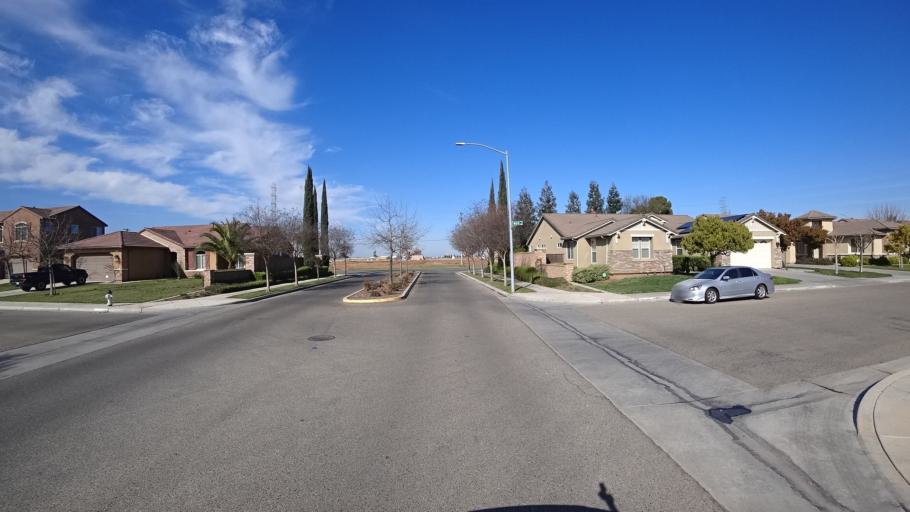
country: US
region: California
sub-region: Fresno County
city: West Park
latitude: 36.7959
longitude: -119.8976
